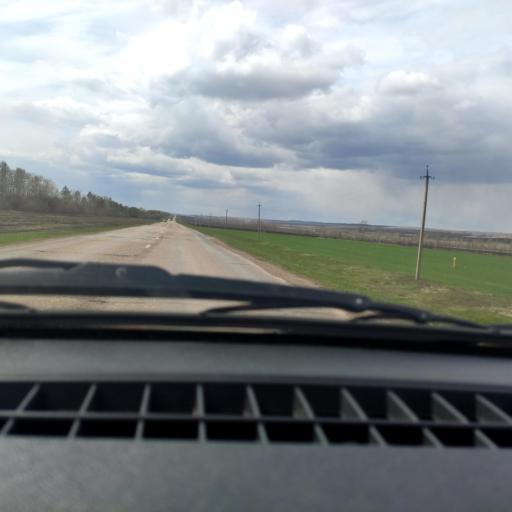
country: RU
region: Bashkortostan
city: Chekmagush
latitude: 55.1087
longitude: 54.9582
